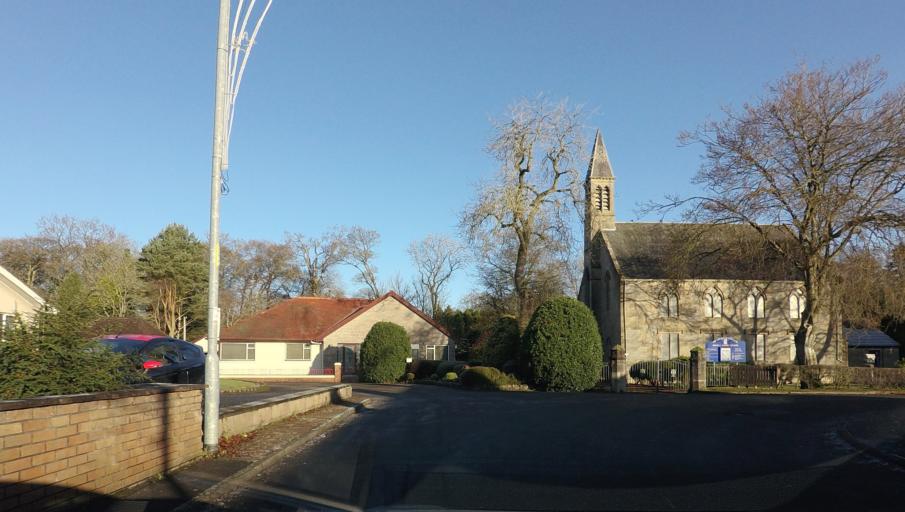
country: GB
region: Scotland
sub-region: North Lanarkshire
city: Newmains
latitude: 55.7922
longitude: -3.8568
